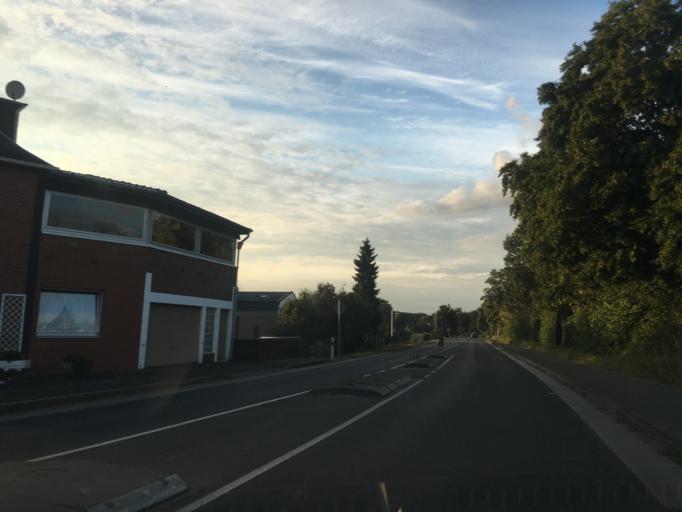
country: DE
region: North Rhine-Westphalia
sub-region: Regierungsbezirk Koln
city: Linnich
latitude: 50.9990
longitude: 6.2761
